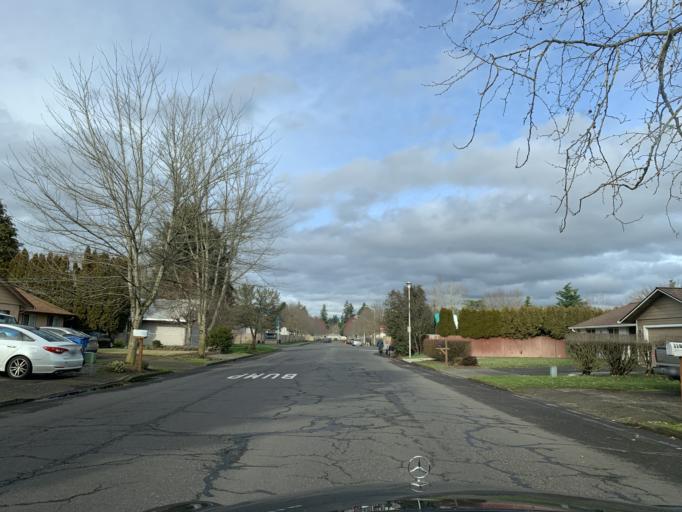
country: US
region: Washington
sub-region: Clark County
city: Mill Plain
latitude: 45.6204
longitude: -122.5138
